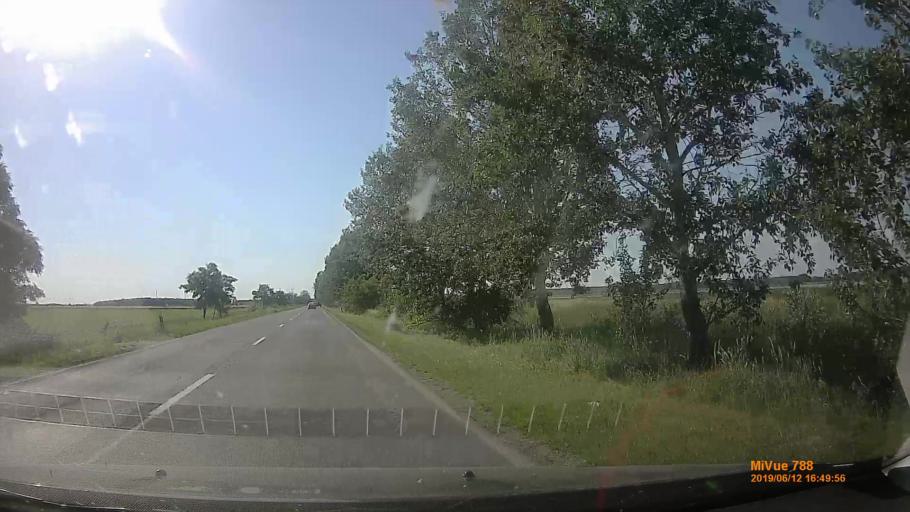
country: HU
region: Csongrad
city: Kiszombor
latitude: 46.1960
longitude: 20.4028
